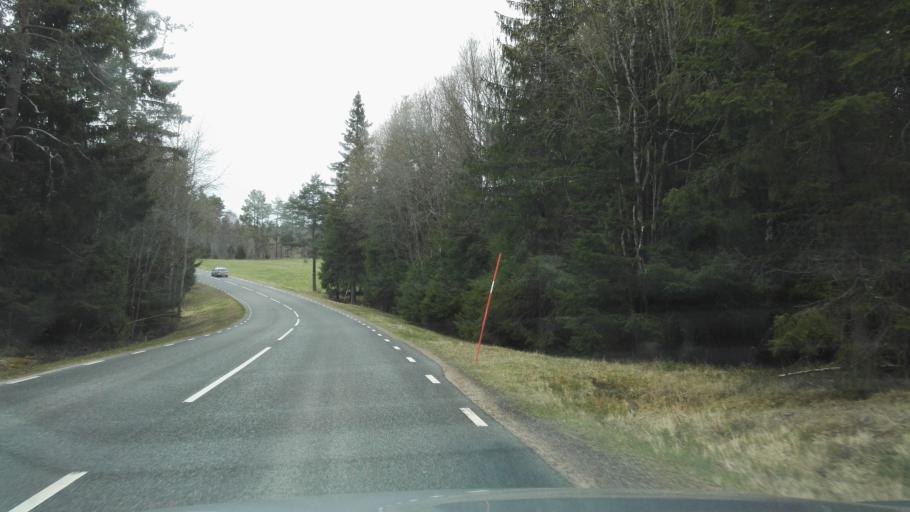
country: SE
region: Joenkoeping
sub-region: Vetlanda Kommun
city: Landsbro
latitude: 57.2833
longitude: 14.8894
